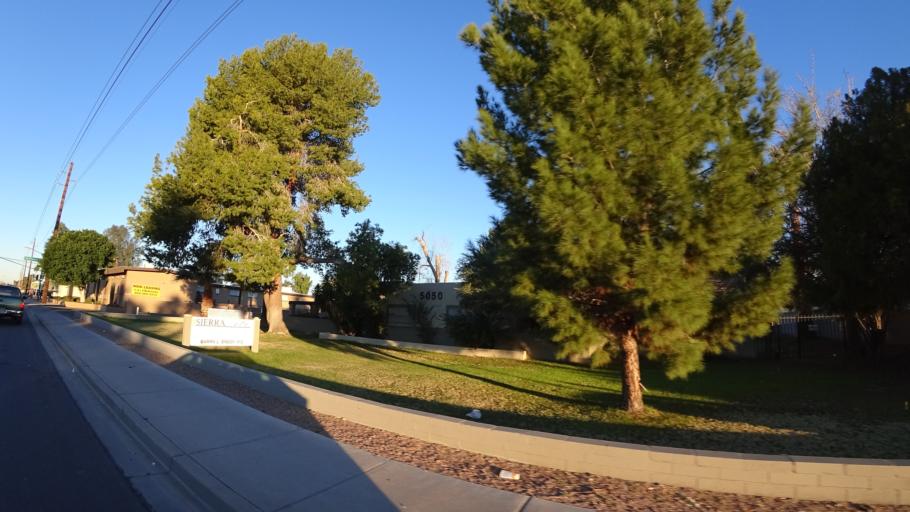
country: US
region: Arizona
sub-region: Maricopa County
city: Paradise Valley
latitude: 33.4801
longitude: -111.9717
